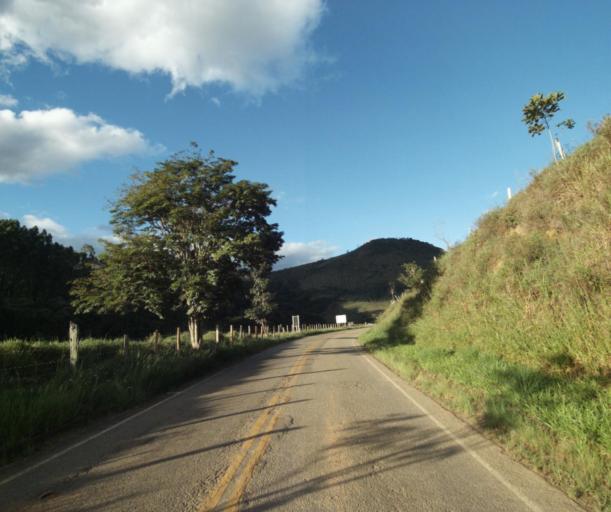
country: BR
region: Espirito Santo
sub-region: Guacui
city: Guacui
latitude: -20.6163
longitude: -41.6801
